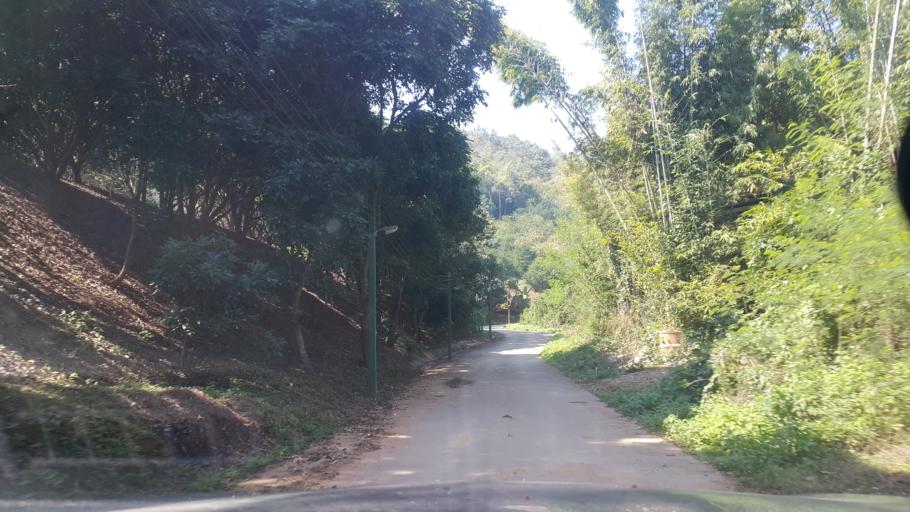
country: TH
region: Chiang Mai
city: Hang Dong
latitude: 18.7504
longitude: 98.8786
